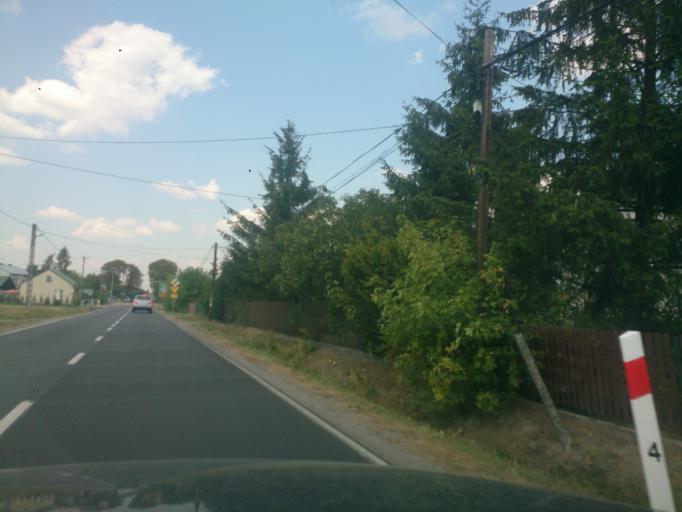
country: PL
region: Subcarpathian Voivodeship
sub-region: Powiat tarnobrzeski
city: Baranow Sandomierski
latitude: 50.4930
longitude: 21.5461
